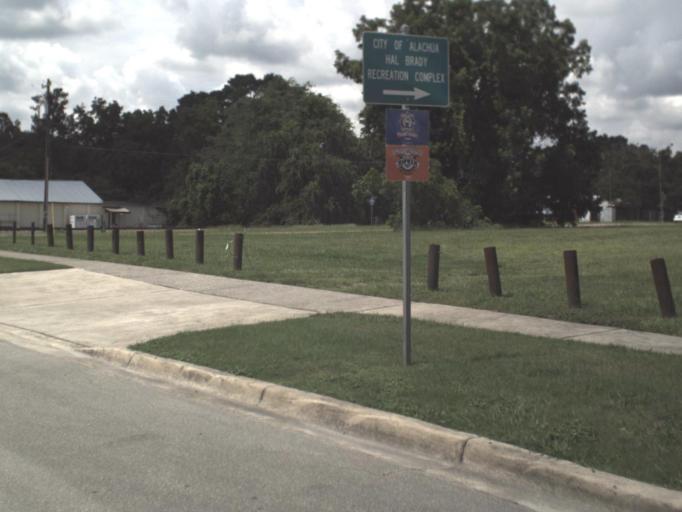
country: US
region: Florida
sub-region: Alachua County
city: Alachua
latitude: 29.7882
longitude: -82.4942
